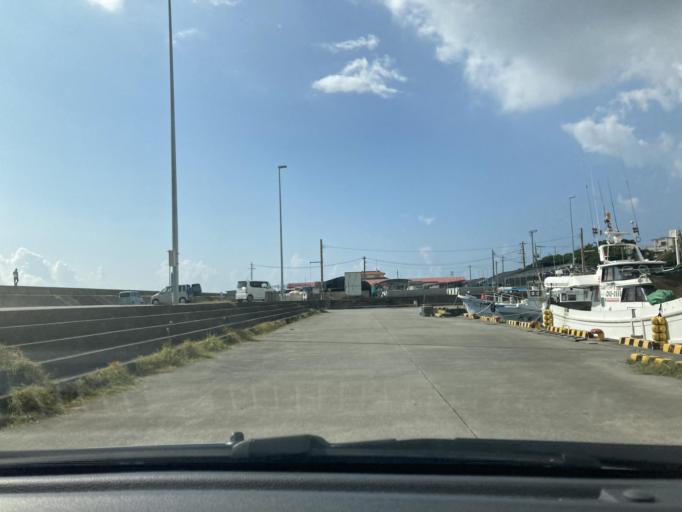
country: JP
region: Okinawa
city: Itoman
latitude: 26.1315
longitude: 127.7764
